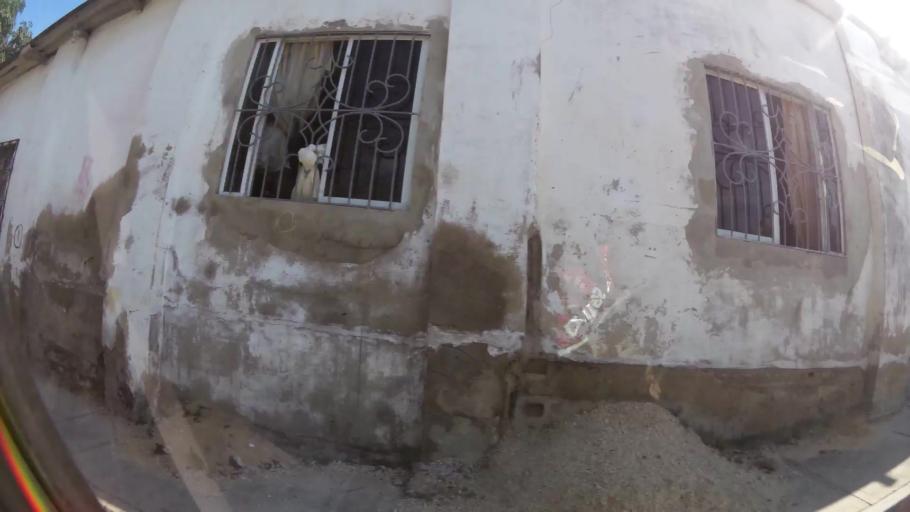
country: CO
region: Atlantico
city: Soledad
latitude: 10.9283
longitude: -74.8171
